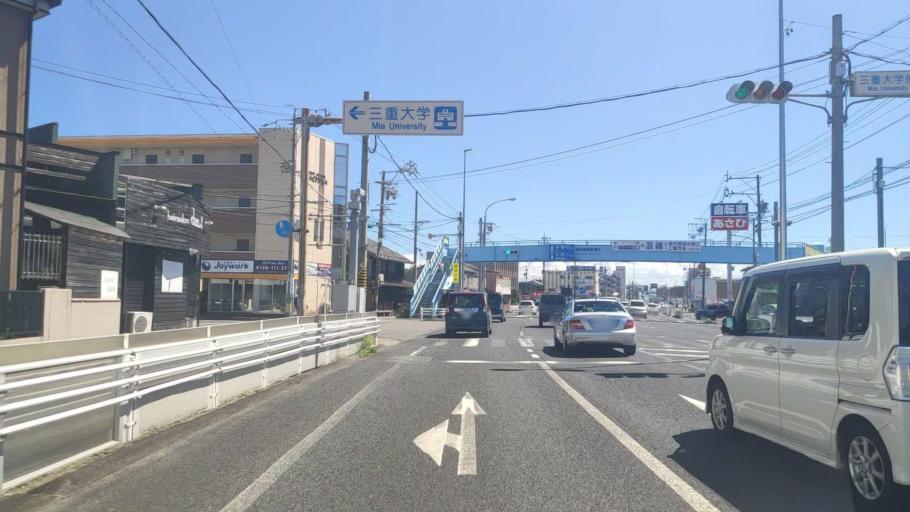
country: JP
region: Mie
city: Tsu-shi
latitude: 34.7474
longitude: 136.5208
